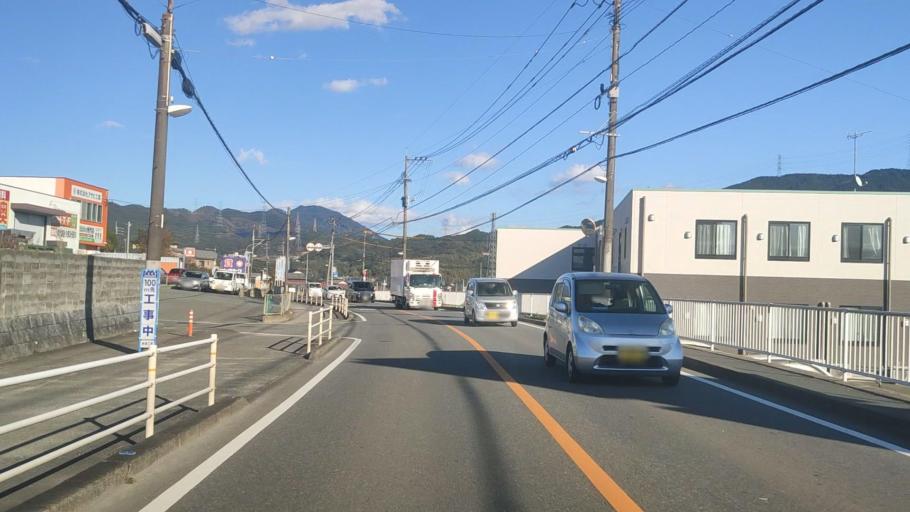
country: JP
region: Fukuoka
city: Dazaifu
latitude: 33.4955
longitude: 130.5441
